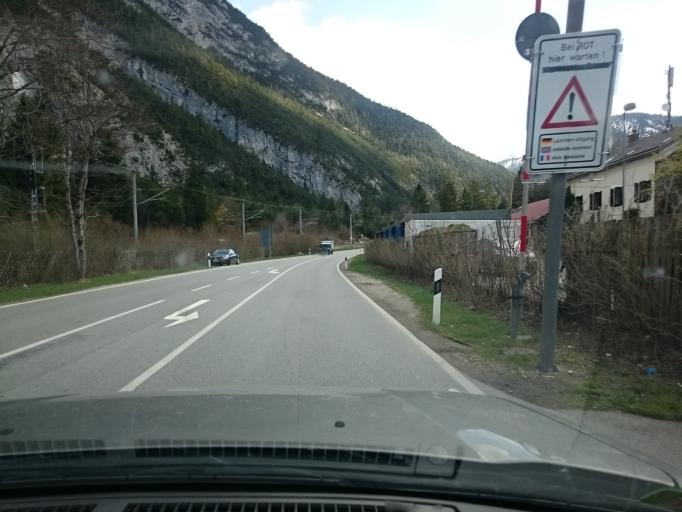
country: AT
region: Tyrol
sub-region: Politischer Bezirk Innsbruck Land
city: Scharnitz
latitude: 47.3994
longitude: 11.2664
